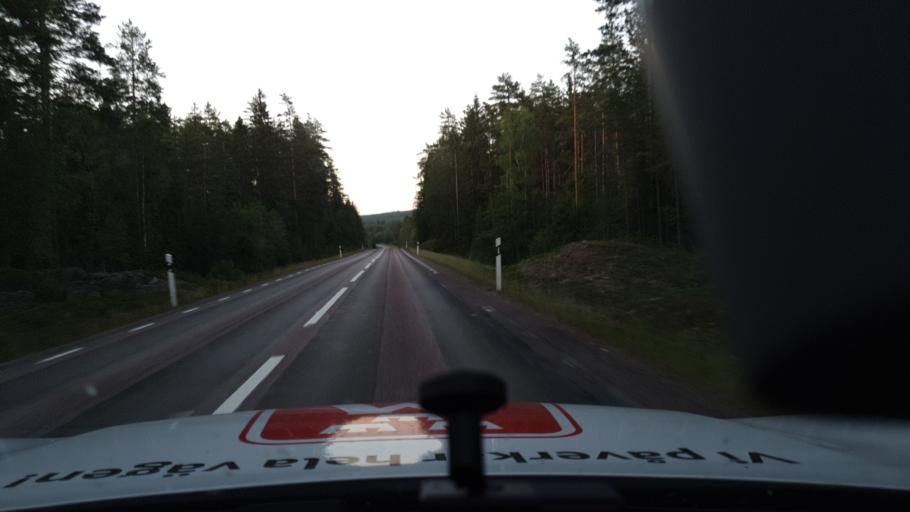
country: SE
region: Vaermland
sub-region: Torsby Kommun
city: Torsby
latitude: 60.3200
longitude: 13.1138
